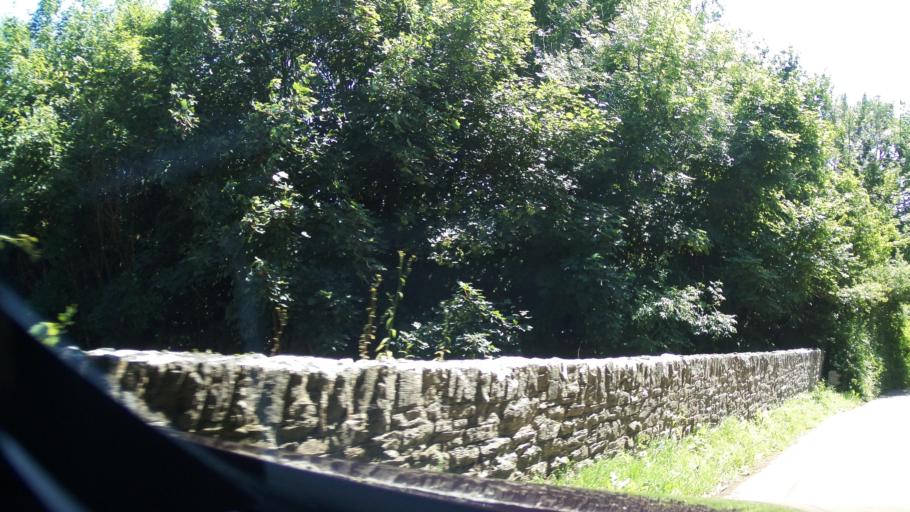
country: GB
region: England
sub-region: Devon
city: Dartmouth
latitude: 50.3891
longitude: -3.5692
